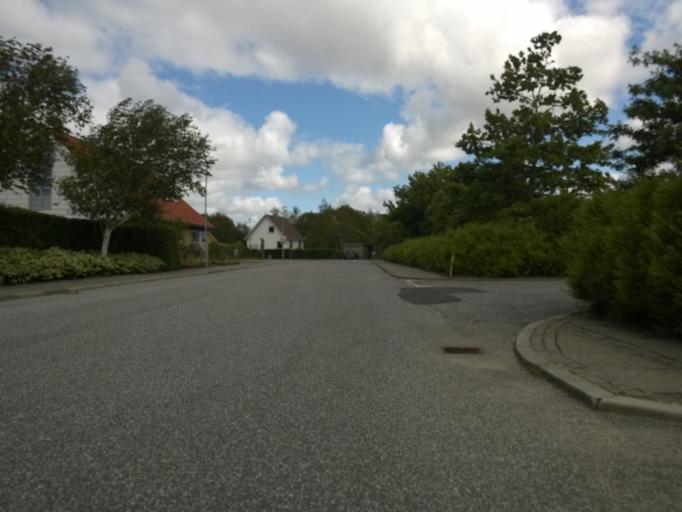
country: DK
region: Central Jutland
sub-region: Holstebro Kommune
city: Vinderup
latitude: 56.4770
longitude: 8.7860
